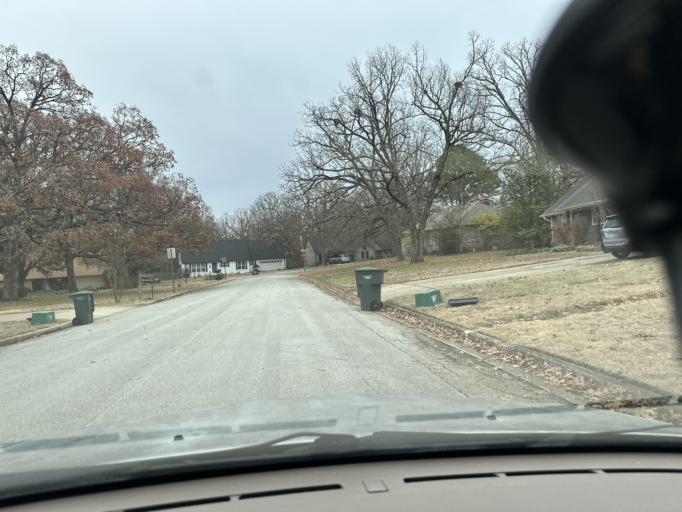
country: US
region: Arkansas
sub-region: Washington County
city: Johnson
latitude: 36.1046
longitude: -94.1423
